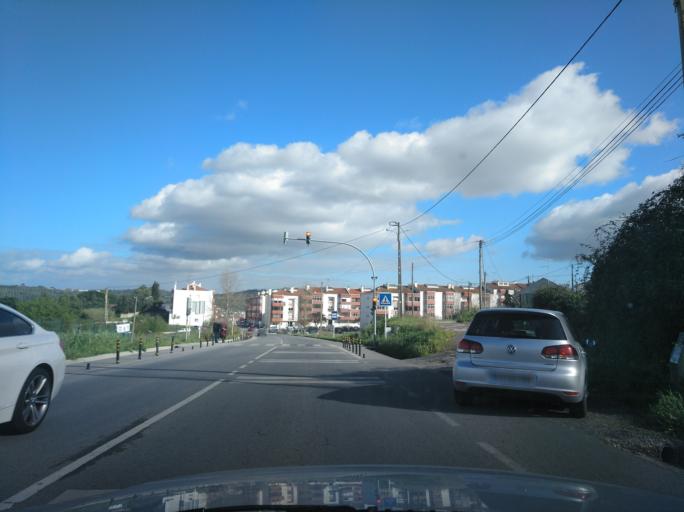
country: PT
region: Lisbon
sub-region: Loures
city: Loures
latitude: 38.8253
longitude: -9.1679
